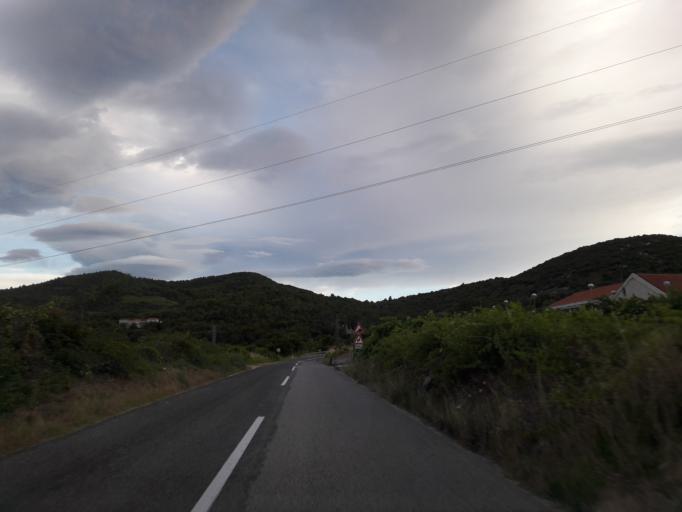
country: HR
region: Dubrovacko-Neretvanska
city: Blato
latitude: 42.9157
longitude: 17.4294
